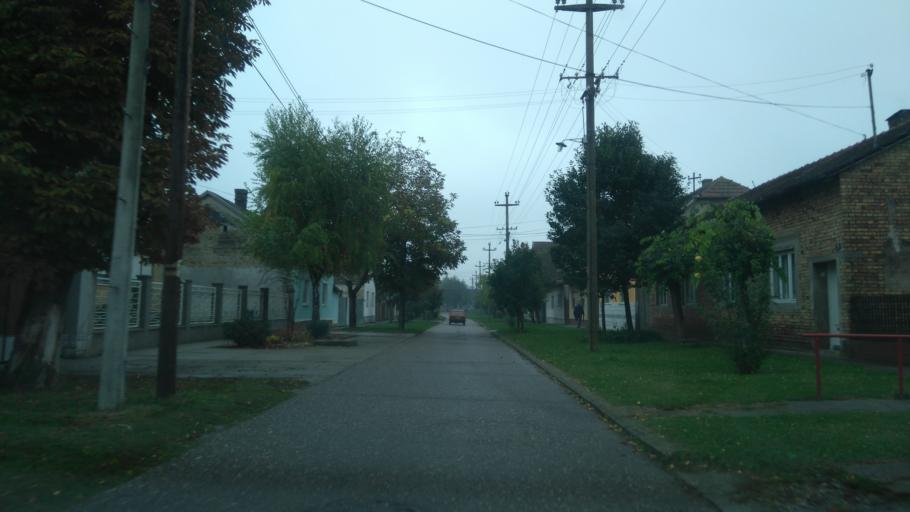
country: RS
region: Autonomna Pokrajina Vojvodina
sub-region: Juznobacki Okrug
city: Becej
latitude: 45.6212
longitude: 20.0505
